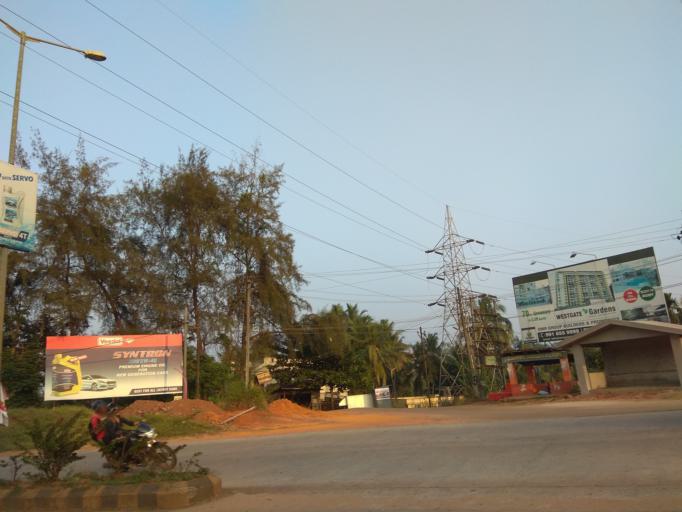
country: IN
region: Karnataka
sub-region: Dakshina Kannada
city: Mangalore
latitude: 12.9285
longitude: 74.8592
